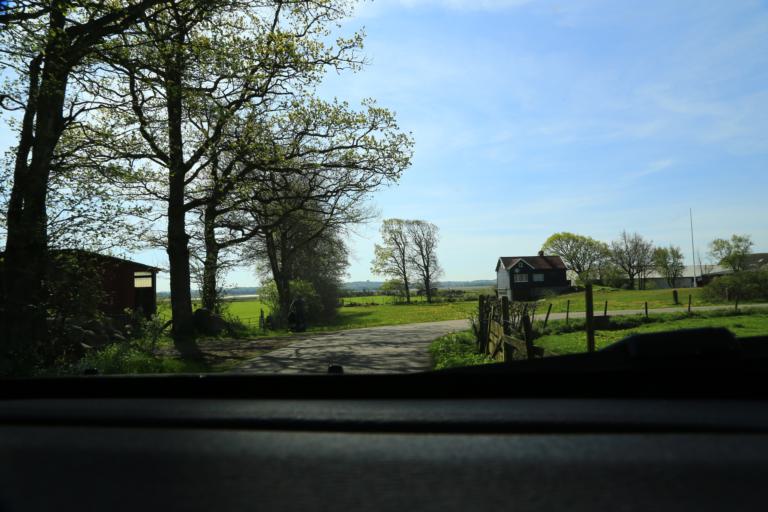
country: SE
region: Halland
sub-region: Varbergs Kommun
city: Varberg
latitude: 57.1418
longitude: 12.2346
